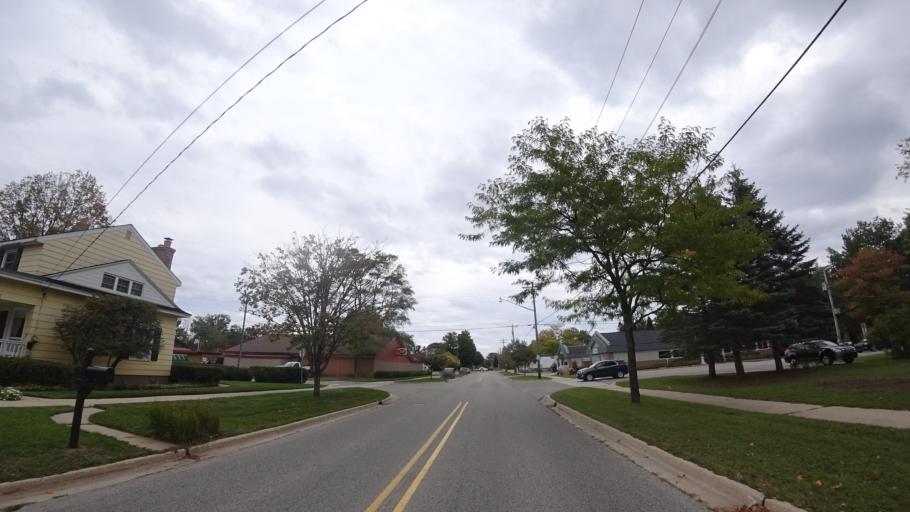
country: US
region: Michigan
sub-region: Emmet County
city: Harbor Springs
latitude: 45.4353
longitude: -84.9937
